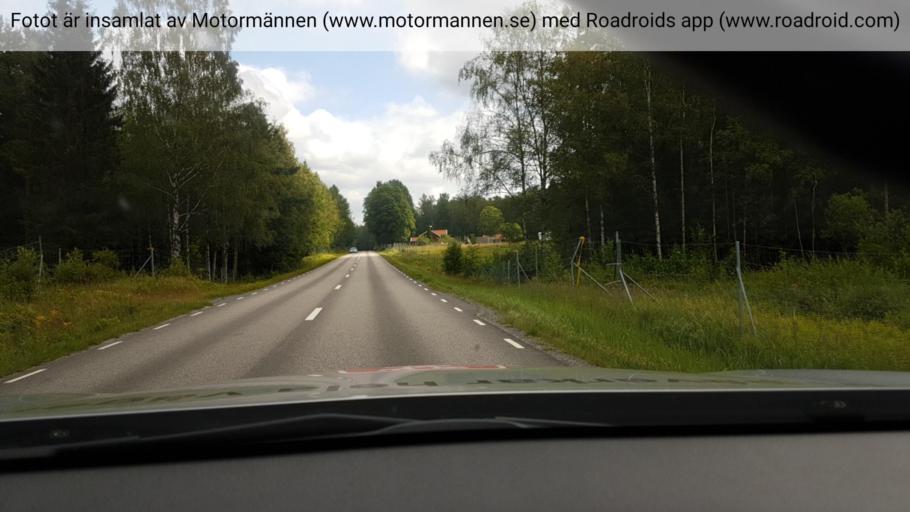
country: SE
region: Vaestra Goetaland
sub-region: Marks Kommun
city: Kinna
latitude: 57.4717
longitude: 12.7632
